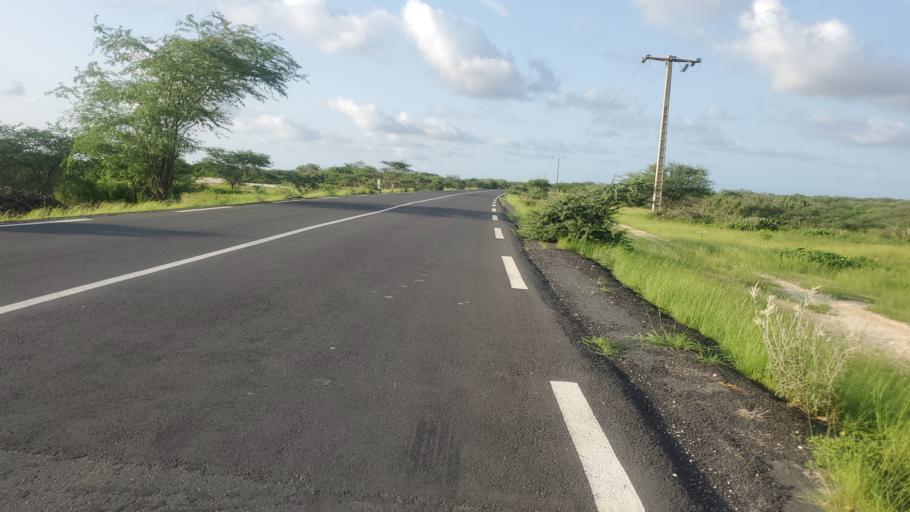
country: SN
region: Saint-Louis
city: Saint-Louis
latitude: 16.1215
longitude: -16.4142
